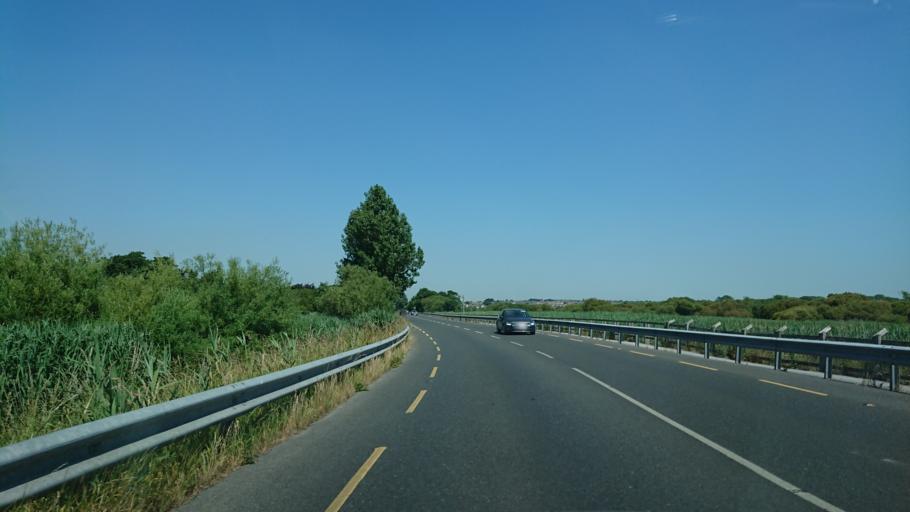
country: IE
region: Munster
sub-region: Waterford
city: Waterford
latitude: 52.2254
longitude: -7.1262
